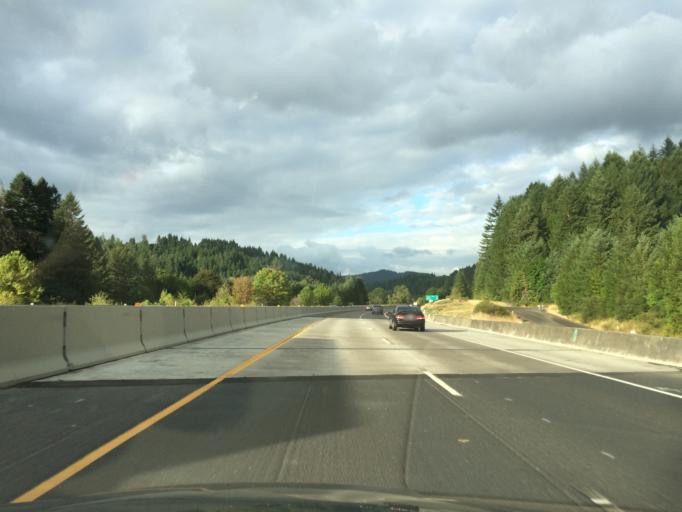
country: US
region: Oregon
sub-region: Douglas County
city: Drain
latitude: 43.7332
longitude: -123.1976
